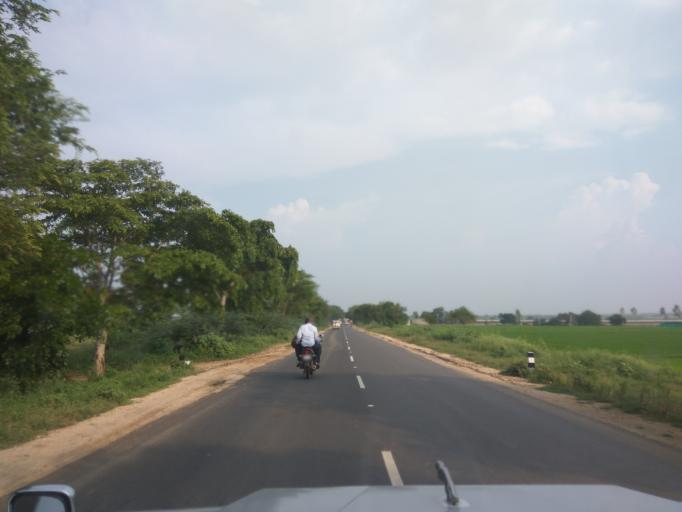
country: IN
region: Andhra Pradesh
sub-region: Guntur
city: Vinukonda
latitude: 16.0057
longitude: 79.6815
